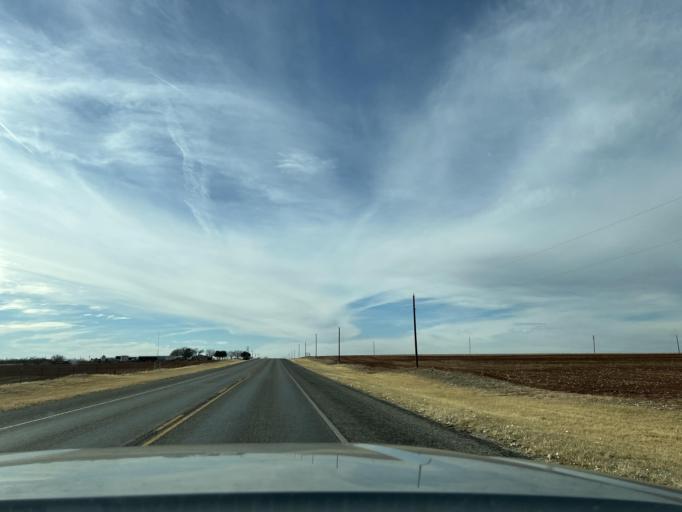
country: US
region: Texas
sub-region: Jones County
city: Anson
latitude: 32.7519
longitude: -99.9421
